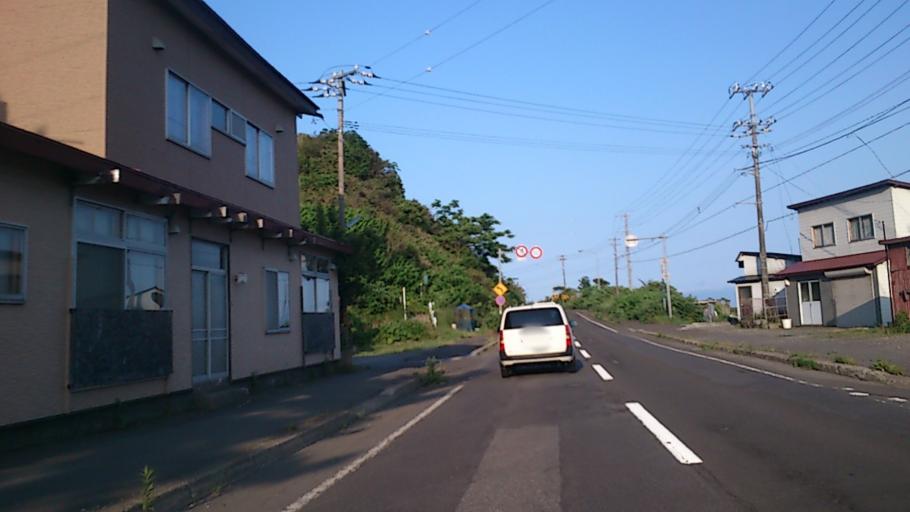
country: JP
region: Hokkaido
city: Kamiiso
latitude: 41.4653
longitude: 140.2497
